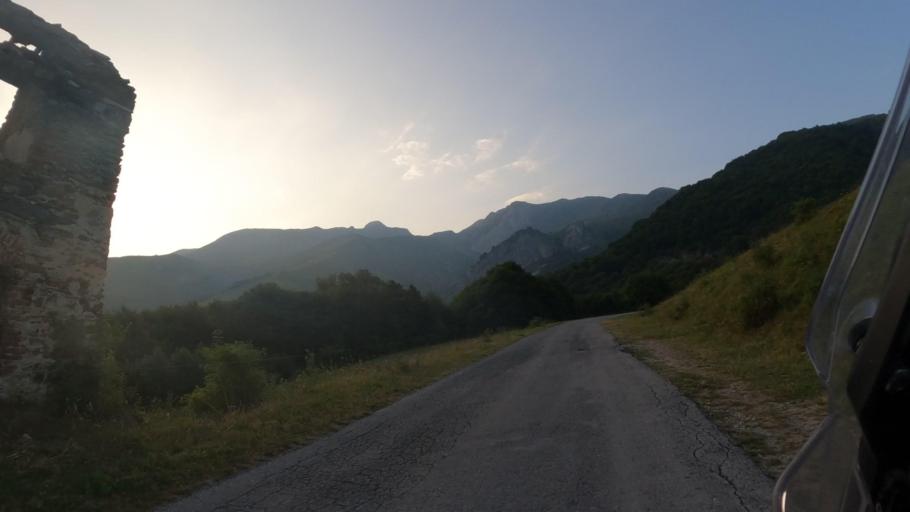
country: IT
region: Piedmont
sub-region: Provincia di Cuneo
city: Limone Piemonte
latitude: 44.1612
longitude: 7.5713
